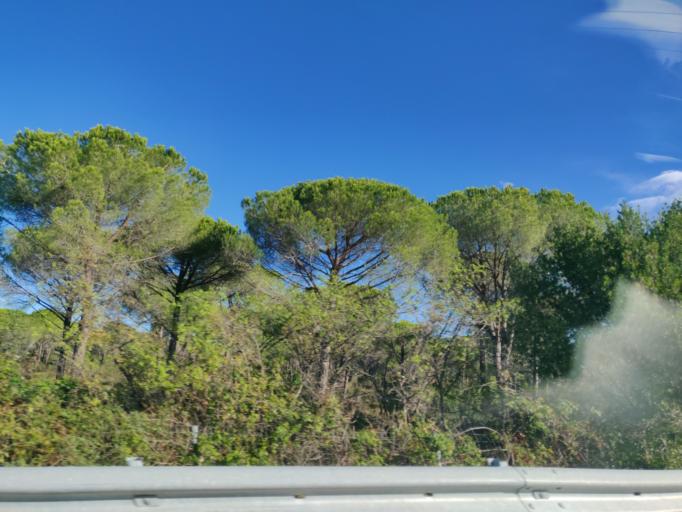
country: IT
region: Tuscany
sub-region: Provincia di Grosseto
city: Scarlino Scalo
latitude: 42.9620
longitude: 10.8375
